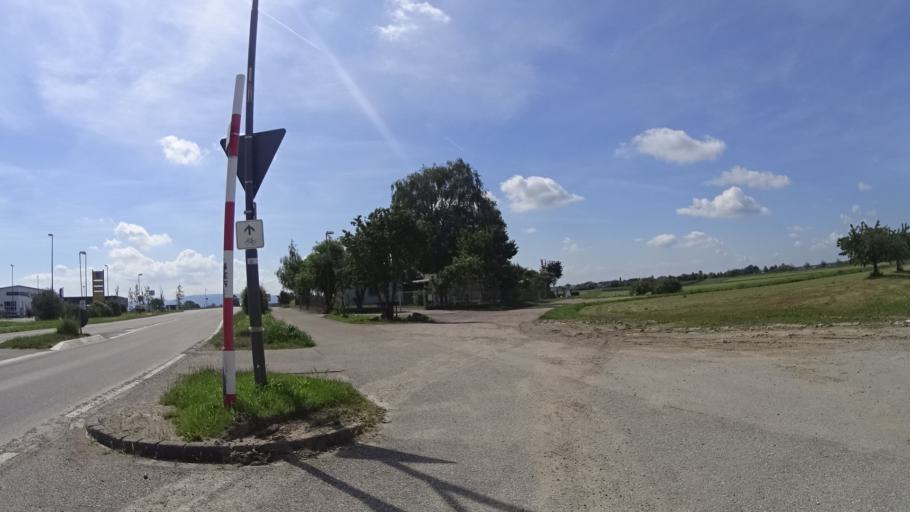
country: DE
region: Baden-Wuerttemberg
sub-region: Freiburg Region
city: Meissenheim
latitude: 48.4606
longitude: 7.8159
